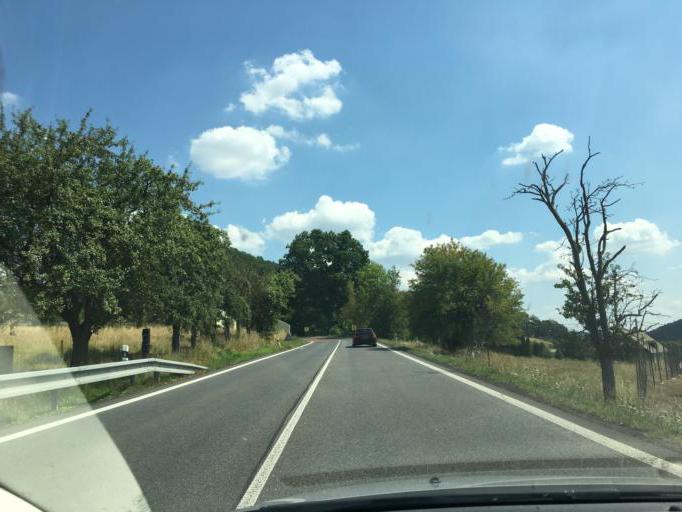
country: CZ
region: Ustecky
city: Ceska Kamenice
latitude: 50.7890
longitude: 14.3715
